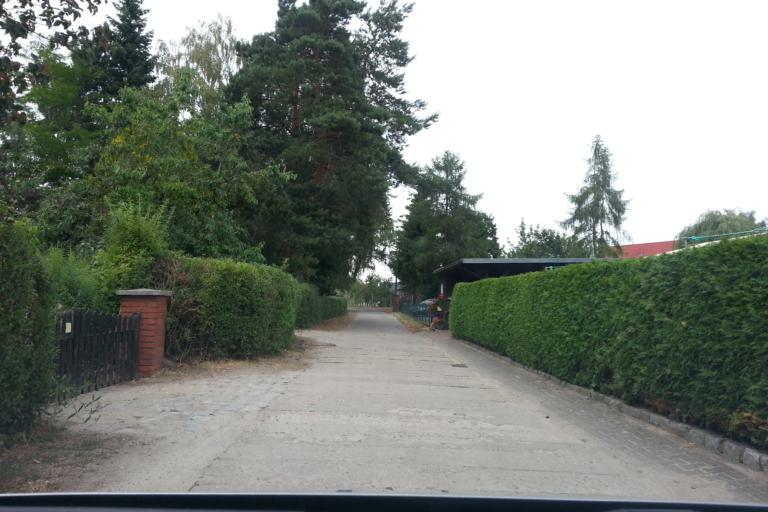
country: DE
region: Mecklenburg-Vorpommern
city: Ferdinandshof
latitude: 53.6614
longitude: 13.8948
